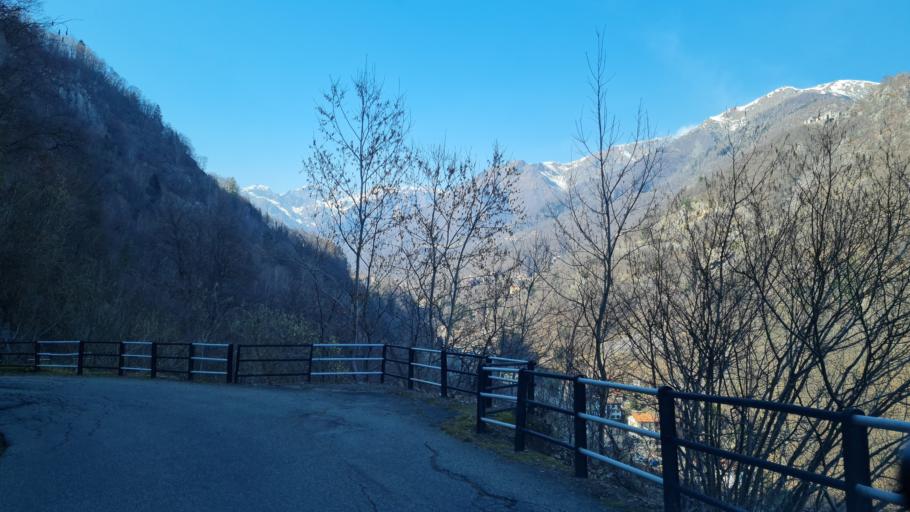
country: IT
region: Piedmont
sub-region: Provincia di Biella
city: San Paolo Cervo
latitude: 45.6436
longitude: 8.0193
